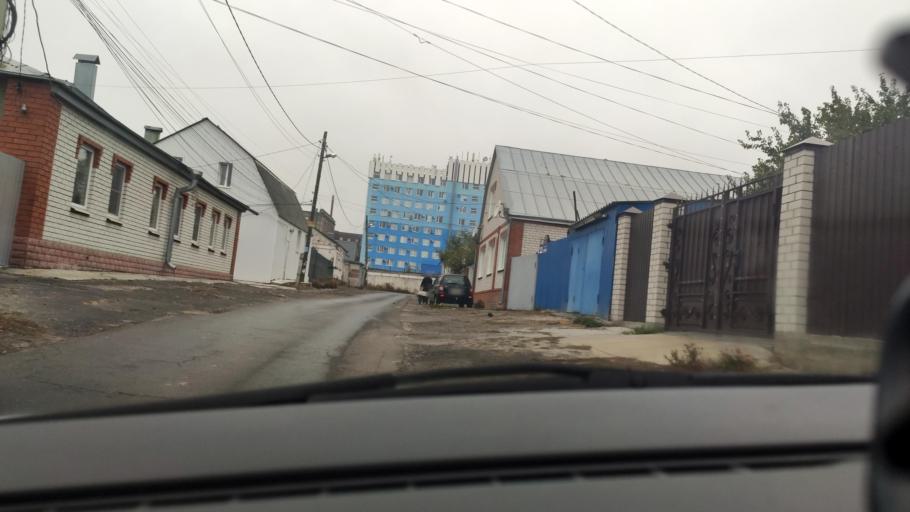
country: RU
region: Voronezj
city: Voronezh
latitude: 51.6836
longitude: 39.2204
